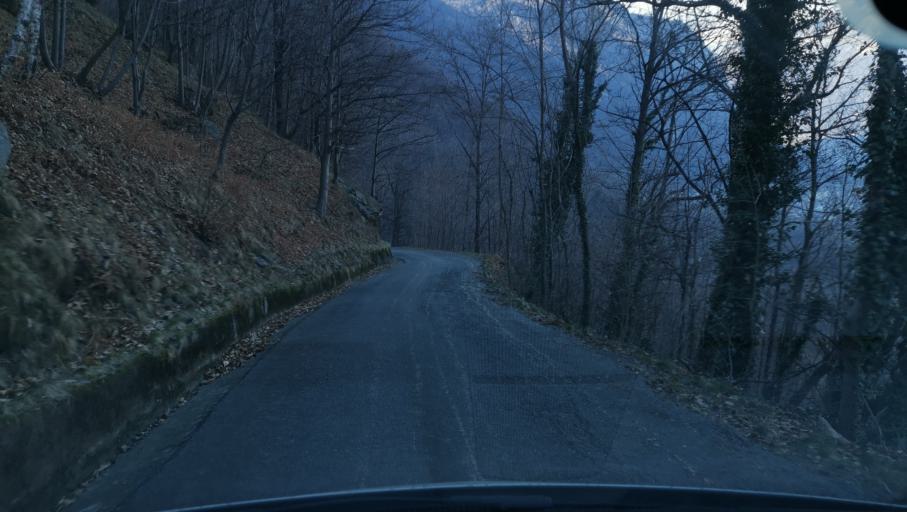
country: IT
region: Piedmont
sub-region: Provincia di Torino
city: Tavagnasco
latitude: 45.5464
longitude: 7.8146
